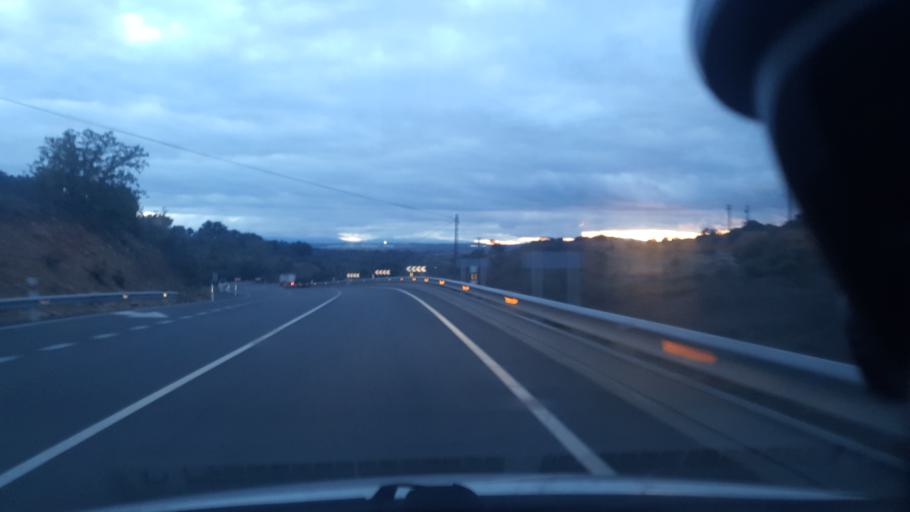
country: ES
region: Castille and Leon
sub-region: Provincia de Avila
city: Ojos-Albos
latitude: 40.7224
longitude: -4.5266
